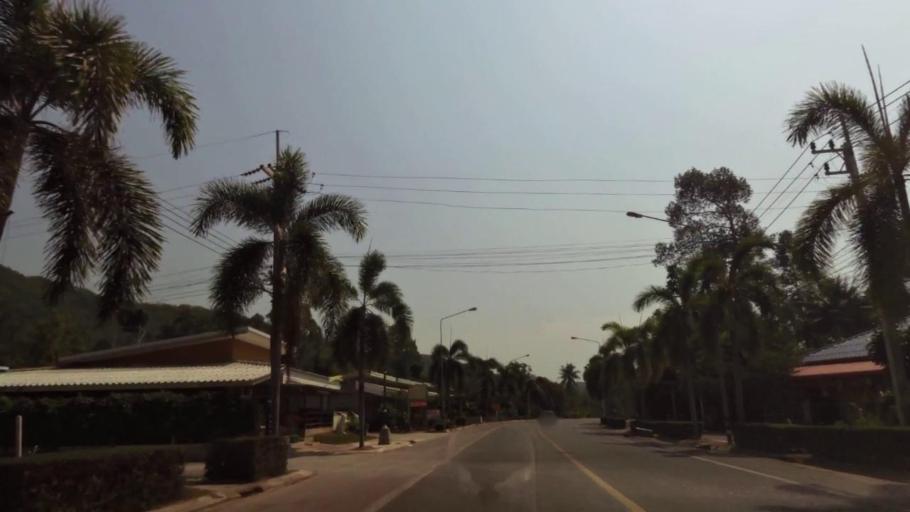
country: TH
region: Chanthaburi
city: Tha Mai
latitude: 12.5351
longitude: 101.9413
